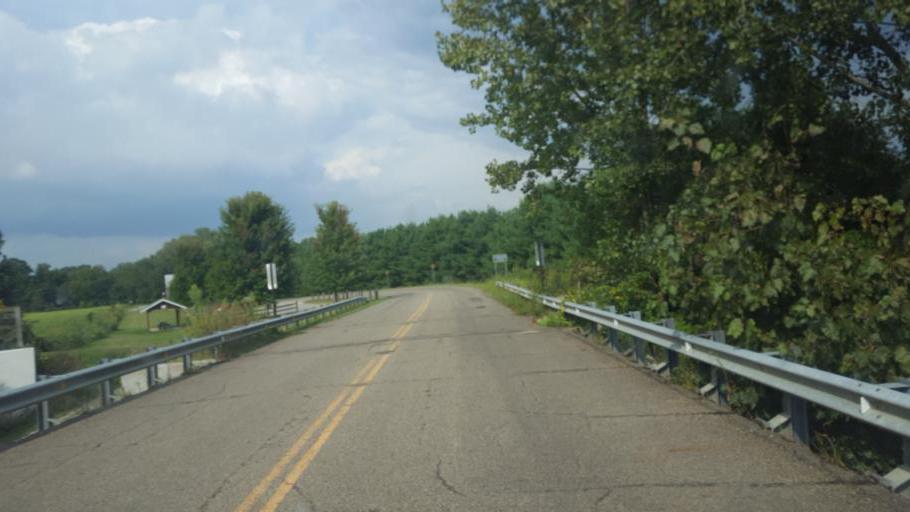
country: US
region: Ohio
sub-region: Knox County
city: Gambier
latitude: 40.3577
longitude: -82.3847
